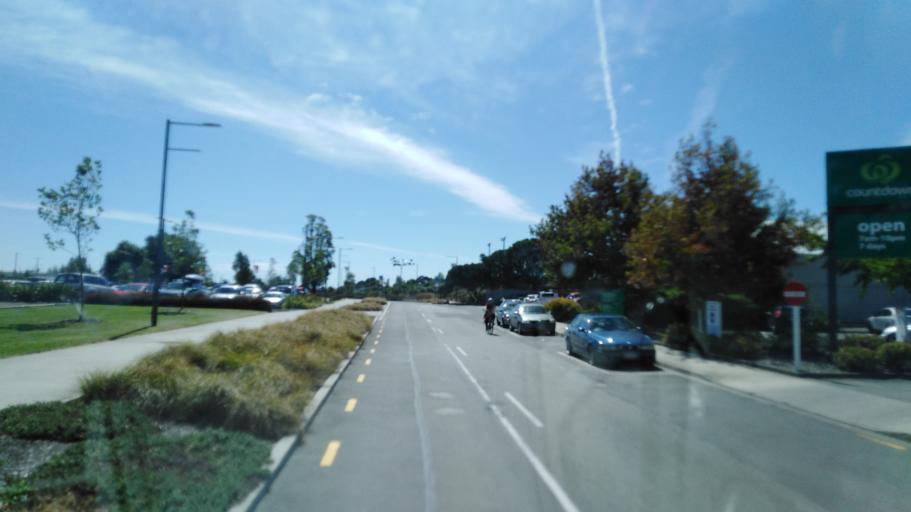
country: NZ
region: Nelson
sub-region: Nelson City
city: Nelson
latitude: -41.2698
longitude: 173.2814
